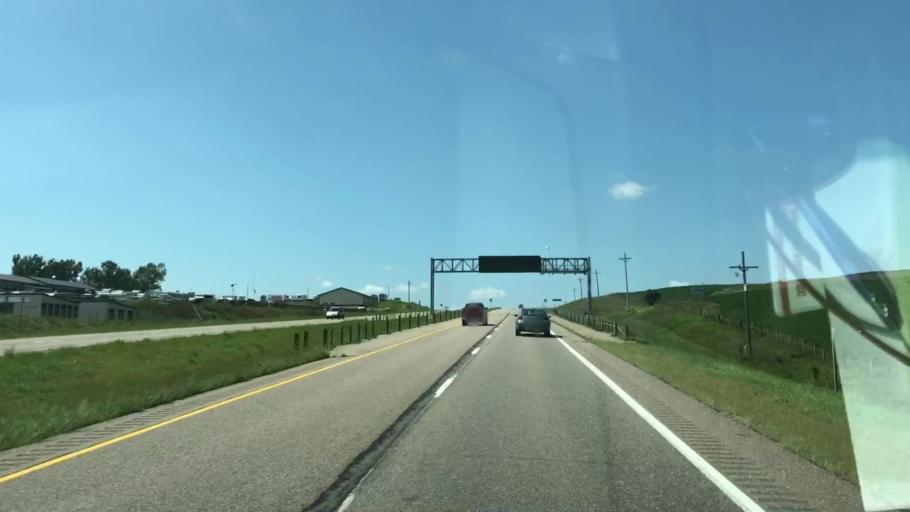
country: US
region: Iowa
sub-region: Woodbury County
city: Sergeant Bluff
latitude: 42.4755
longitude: -96.2924
